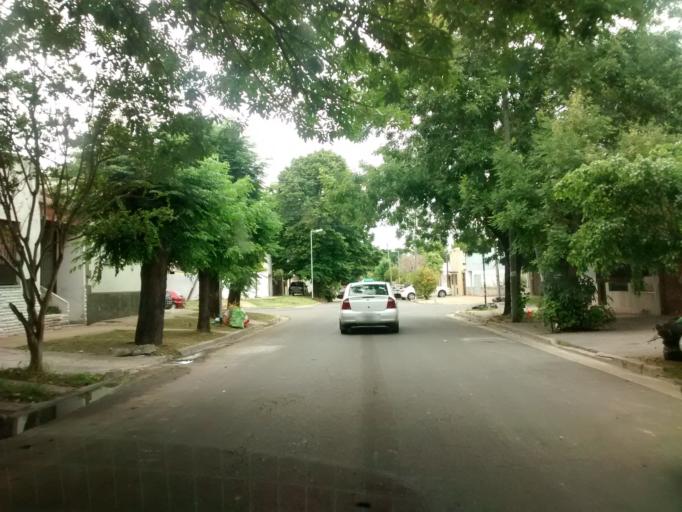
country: AR
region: Buenos Aires
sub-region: Partido de La Plata
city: La Plata
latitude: -34.9315
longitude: -57.9242
